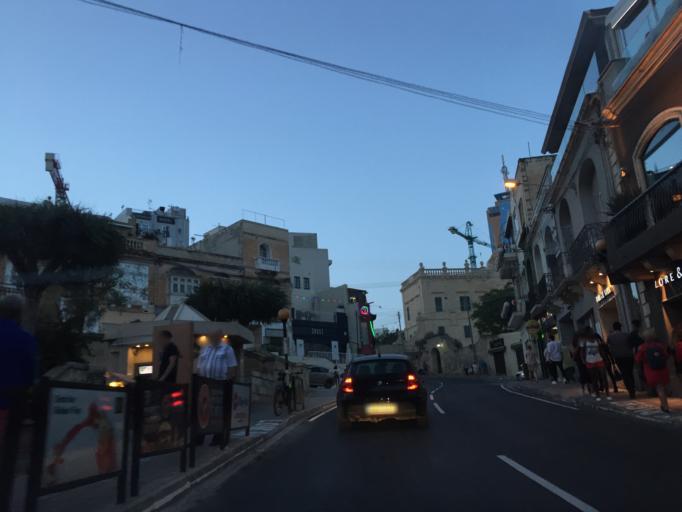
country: MT
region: Saint Julian
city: San Giljan
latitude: 35.9199
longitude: 14.4903
